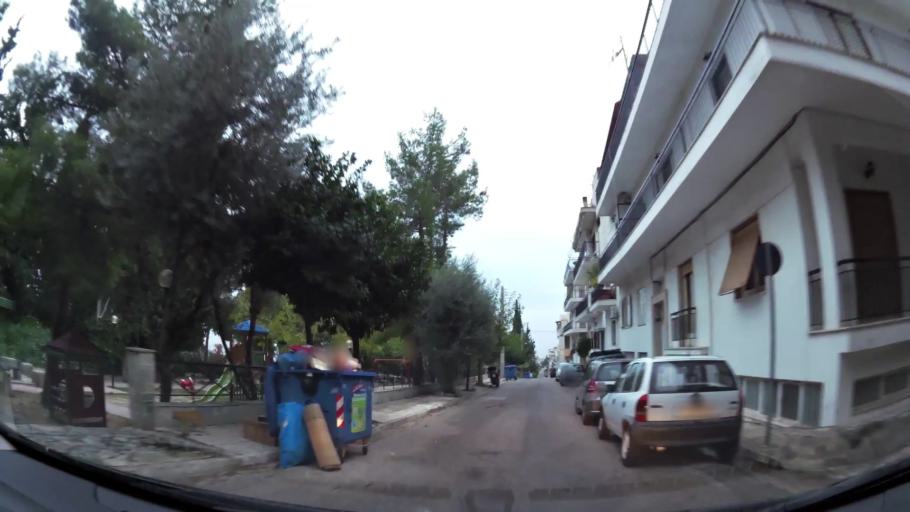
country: GR
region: Attica
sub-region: Nomarchia Athinas
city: Agia Varvara
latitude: 37.9972
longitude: 23.6559
